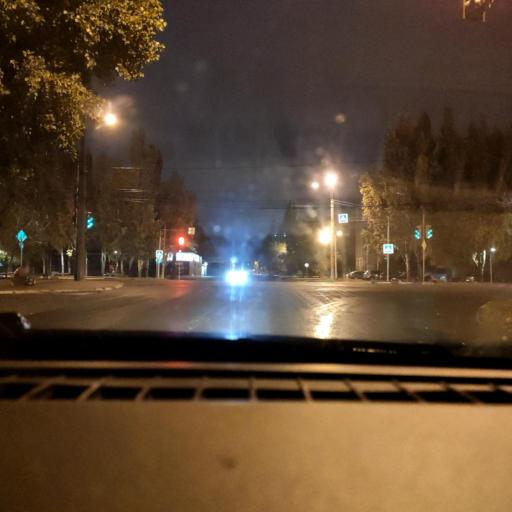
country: RU
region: Voronezj
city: Voronezh
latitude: 51.6708
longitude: 39.2557
